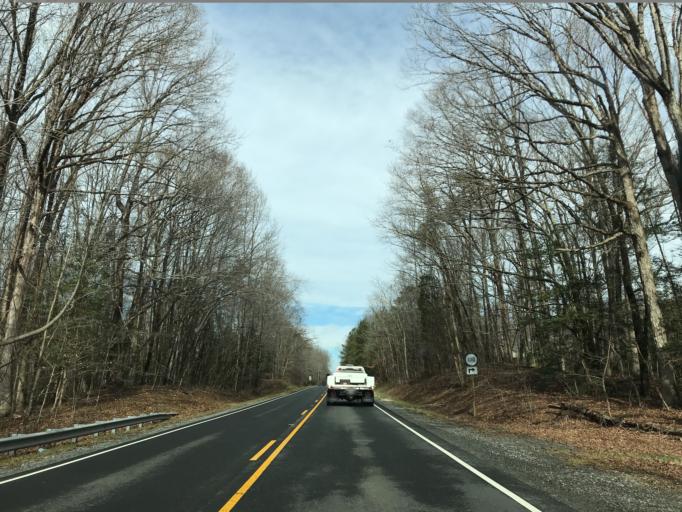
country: US
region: Virginia
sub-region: King George County
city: Dahlgren
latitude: 38.3051
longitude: -77.0752
